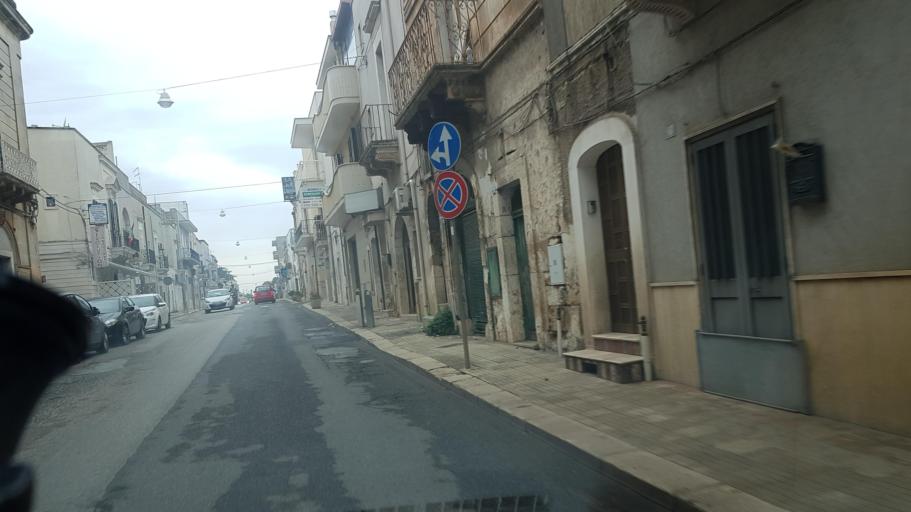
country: IT
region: Apulia
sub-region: Provincia di Brindisi
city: Carovigno
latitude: 40.7037
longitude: 17.6567
